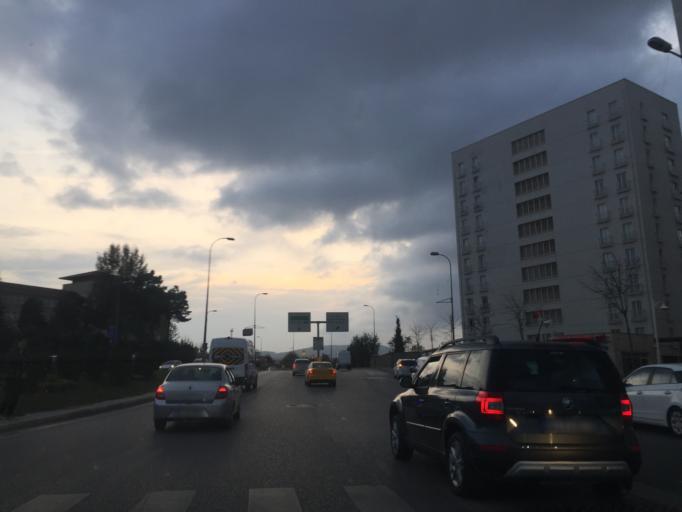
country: TR
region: Istanbul
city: Samandira
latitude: 40.9902
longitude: 29.2280
